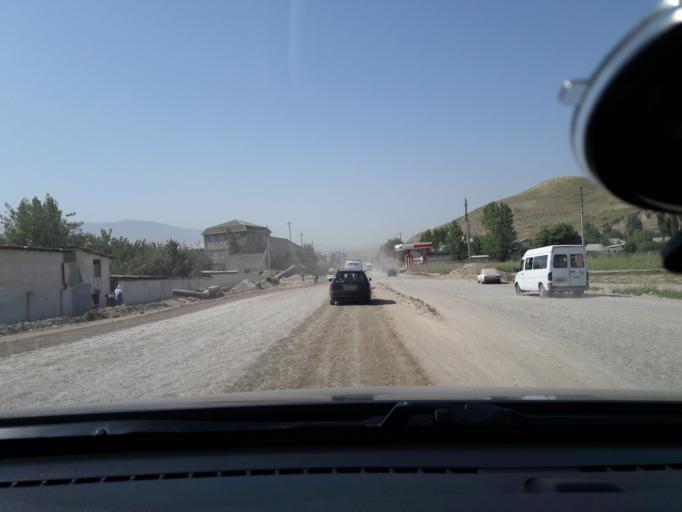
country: TJ
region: Dushanbe
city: Boshkengash
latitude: 38.4469
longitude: 68.7336
